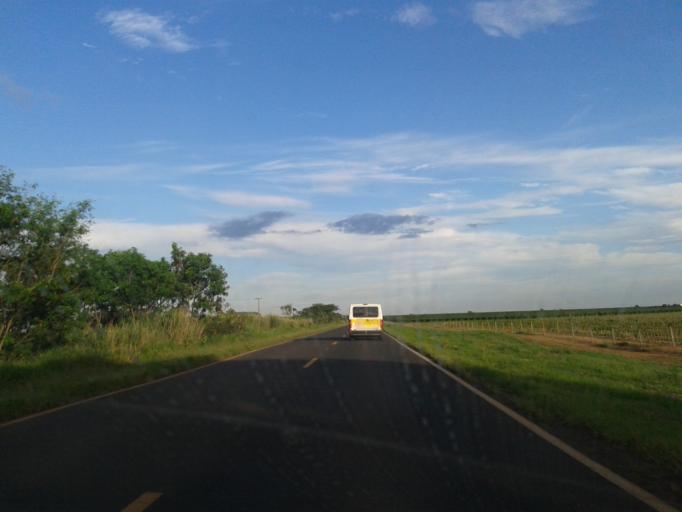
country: BR
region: Minas Gerais
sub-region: Araguari
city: Araguari
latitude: -18.6344
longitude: -48.2288
